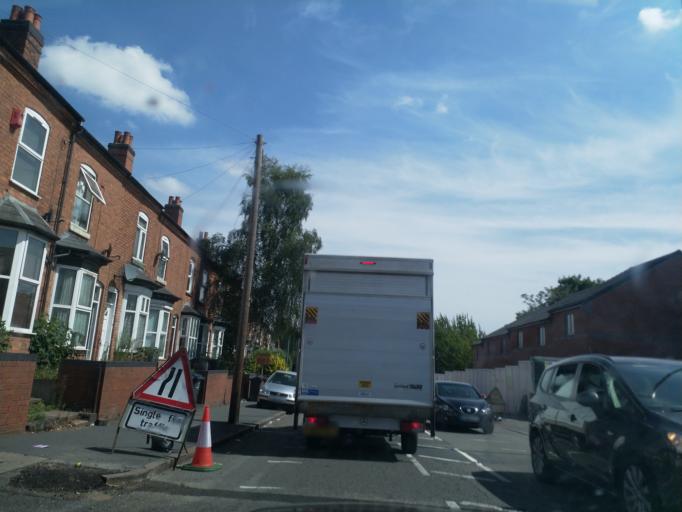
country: GB
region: England
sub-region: City and Borough of Birmingham
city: Hockley
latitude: 52.5158
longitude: -1.9103
